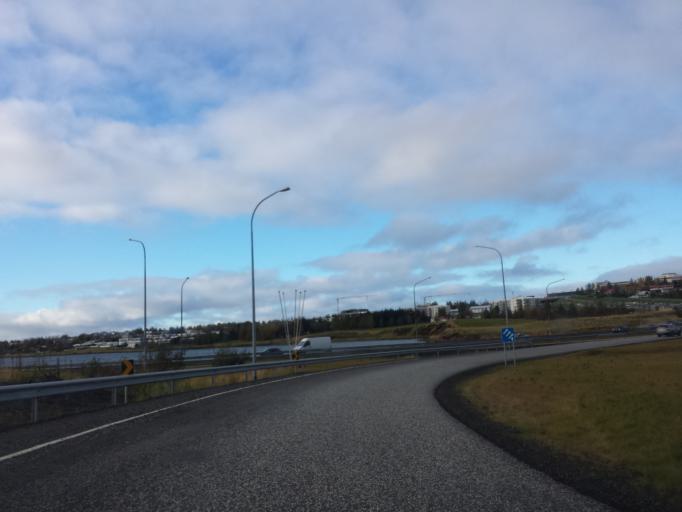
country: IS
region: Capital Region
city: Kopavogur
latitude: 64.1024
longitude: -21.9042
